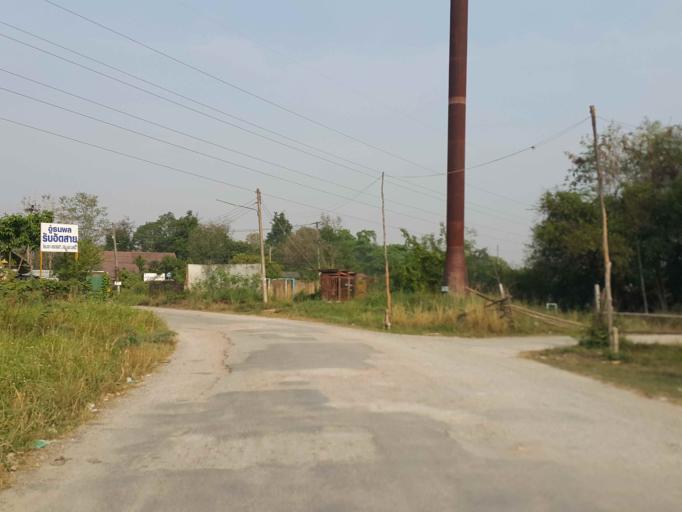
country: TH
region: Chiang Mai
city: San Kamphaeng
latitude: 18.7645
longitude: 99.0653
